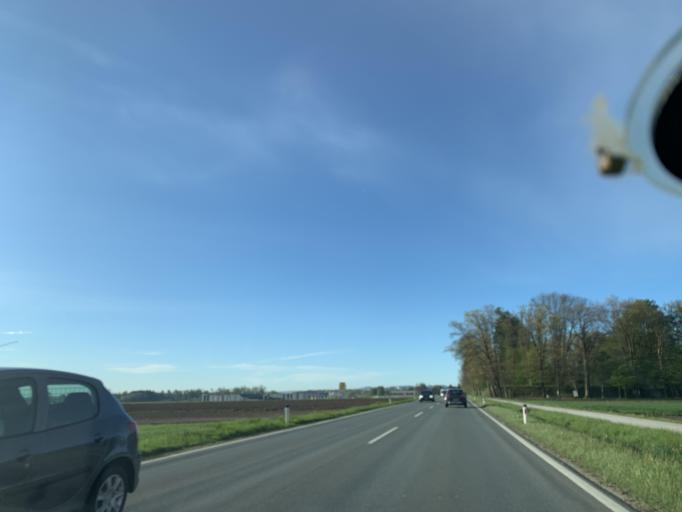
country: AT
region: Styria
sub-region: Politischer Bezirk Leibnitz
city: Lang
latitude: 46.8472
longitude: 15.5161
